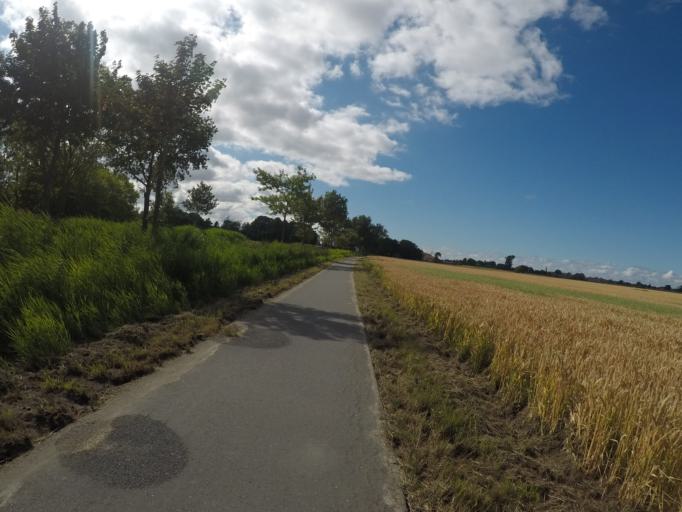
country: DE
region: Lower Saxony
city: Otterndorf
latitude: 53.7912
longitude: 8.9141
